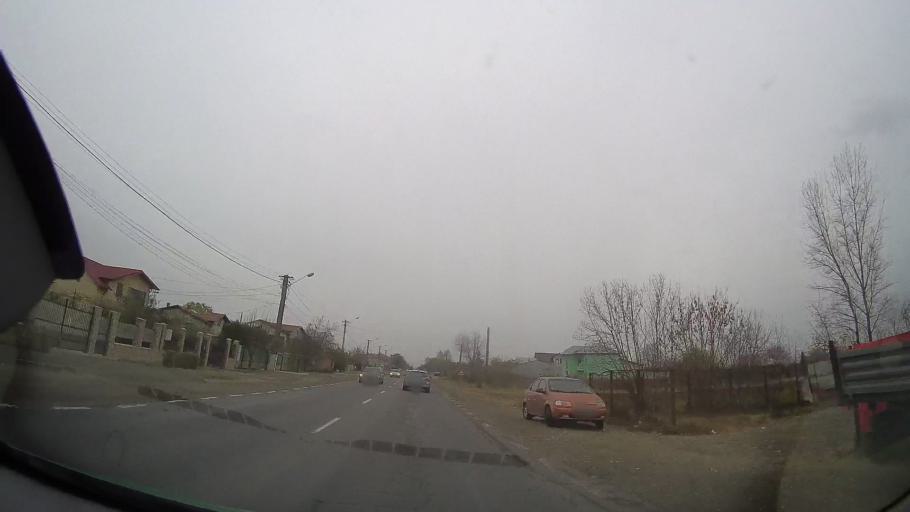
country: RO
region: Prahova
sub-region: Comuna Blejoiu
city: Ploiestiori
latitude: 44.9724
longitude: 26.0213
